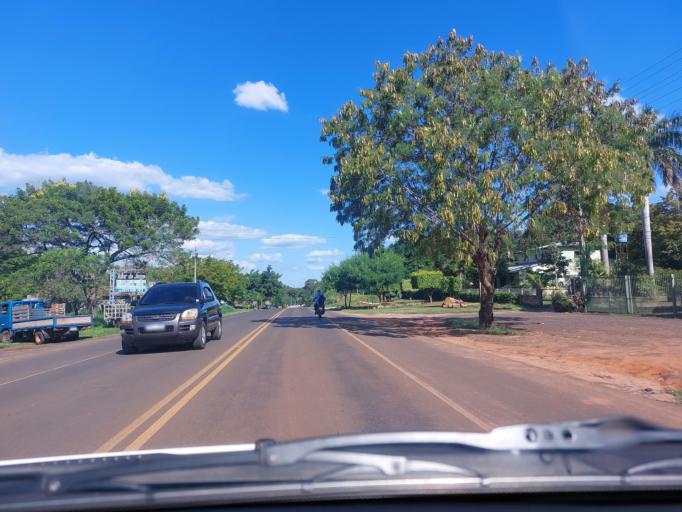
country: PY
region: San Pedro
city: Guayaybi
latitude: -24.6617
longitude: -56.4575
